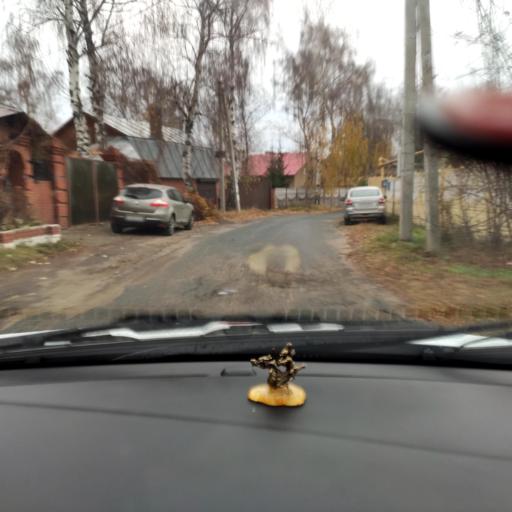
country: RU
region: Tatarstan
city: Vysokaya Gora
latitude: 55.8456
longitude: 49.2382
